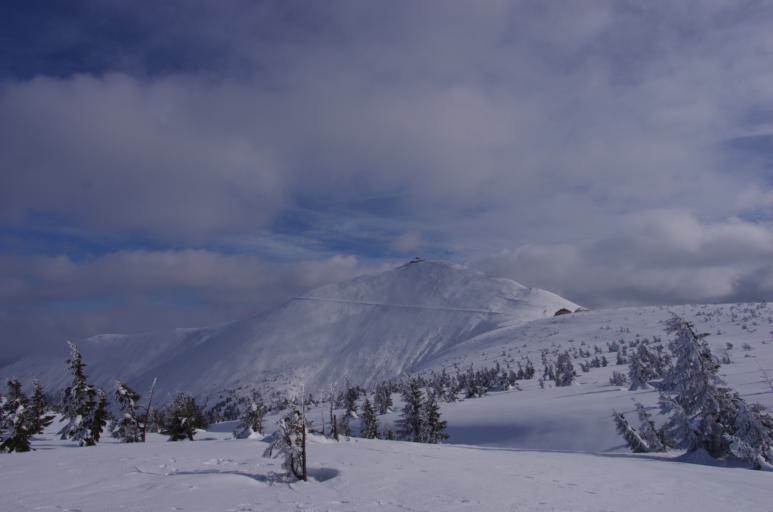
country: PL
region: Lower Silesian Voivodeship
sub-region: Powiat jeleniogorski
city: Karpacz
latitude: 50.7422
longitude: 15.7242
